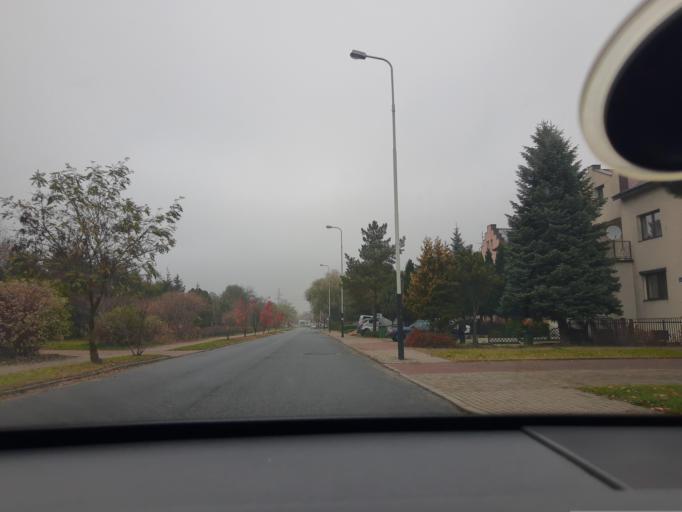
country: PL
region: Lodz Voivodeship
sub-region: Powiat pabianicki
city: Konstantynow Lodzki
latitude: 51.7443
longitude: 19.3778
